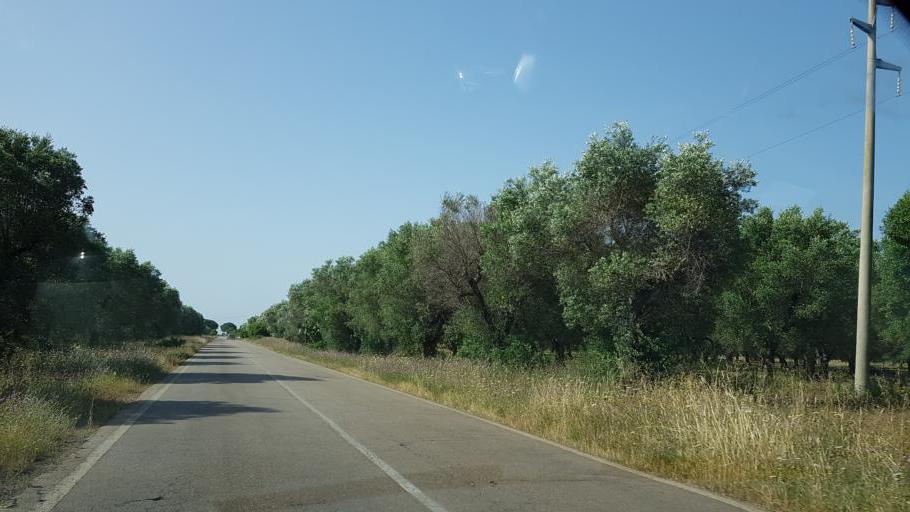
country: IT
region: Apulia
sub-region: Provincia di Brindisi
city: San Pancrazio Salentino
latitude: 40.3500
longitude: 17.8459
